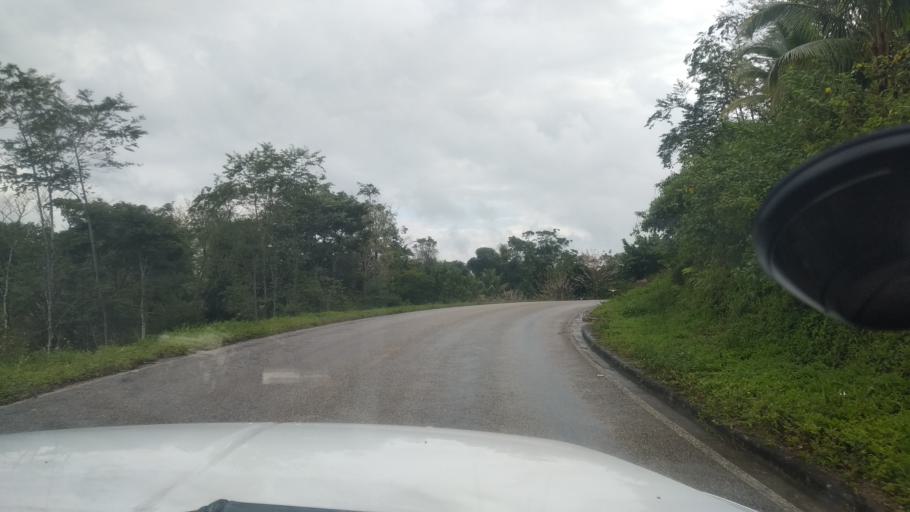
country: GT
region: Peten
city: San Luis
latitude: 16.2054
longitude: -89.1426
